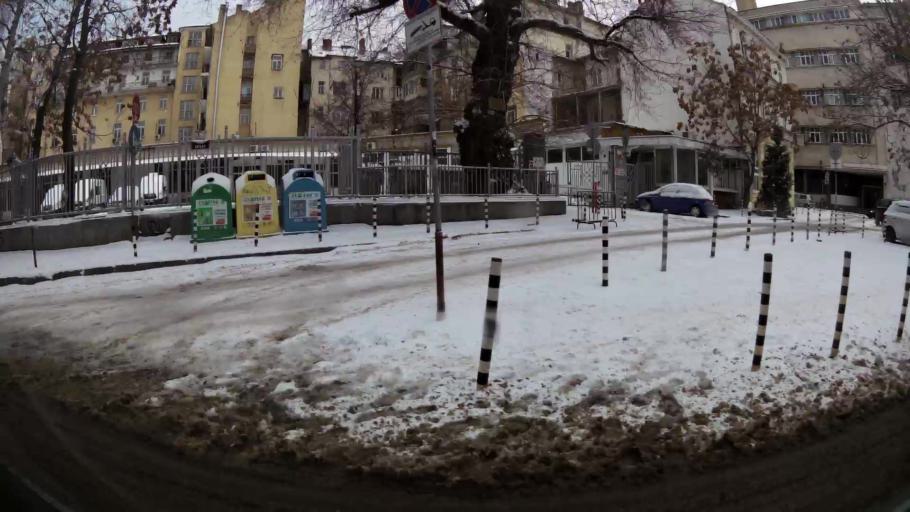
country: BG
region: Sofia-Capital
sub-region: Stolichna Obshtina
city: Sofia
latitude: 42.6995
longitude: 23.3250
